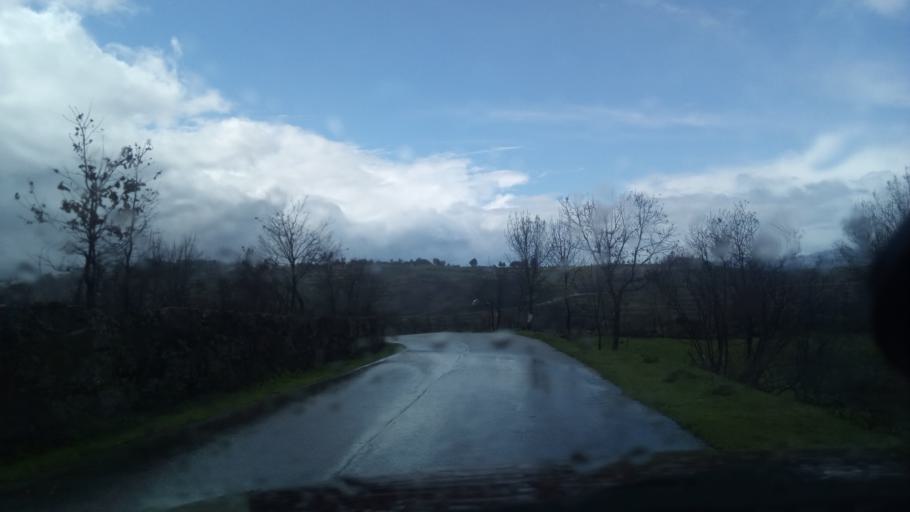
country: PT
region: Guarda
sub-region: Fornos de Algodres
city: Fornos de Algodres
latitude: 40.5514
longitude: -7.4744
